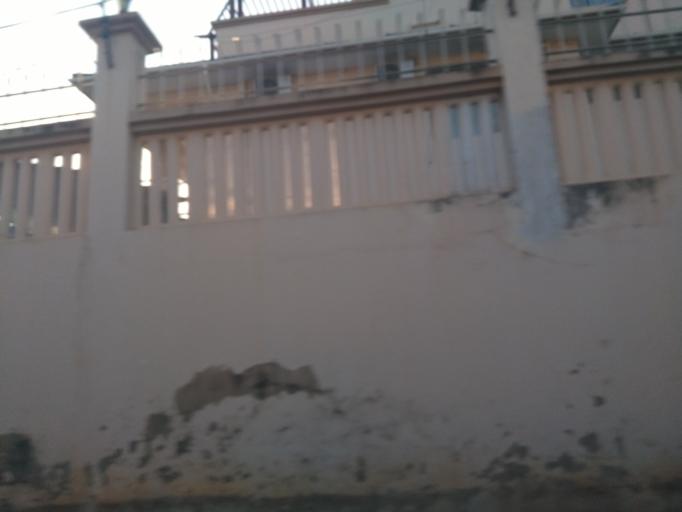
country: TZ
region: Dar es Salaam
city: Magomeni
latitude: -6.7611
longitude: 39.2564
